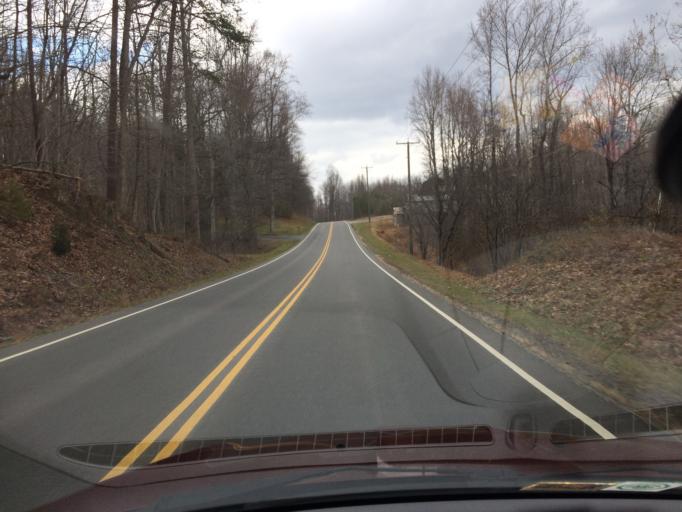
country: US
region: Virginia
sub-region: Patrick County
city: Stuart
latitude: 36.7390
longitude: -80.2501
